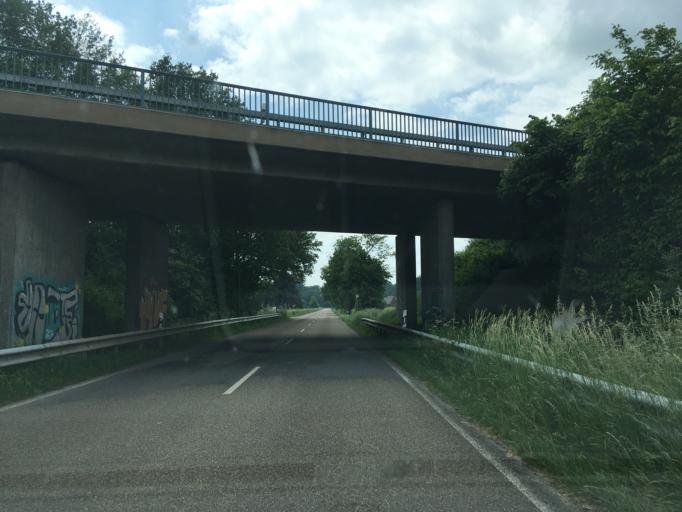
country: DE
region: North Rhine-Westphalia
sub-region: Regierungsbezirk Munster
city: Sudlohn
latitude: 51.9257
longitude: 6.8738
